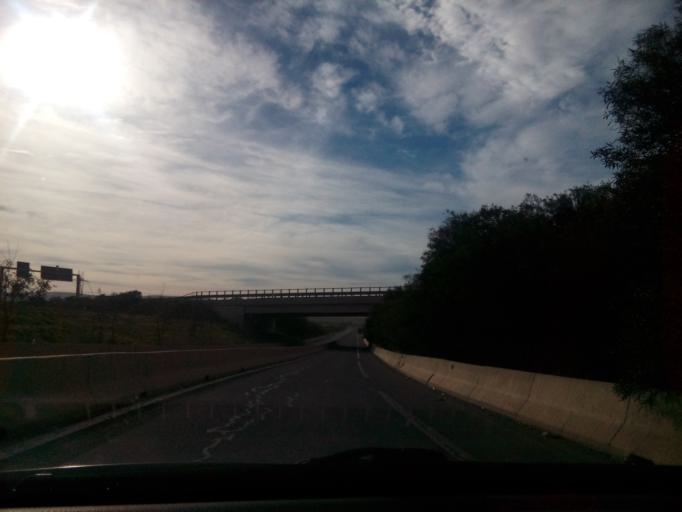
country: DZ
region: Oran
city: Sidi ech Chahmi
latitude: 35.5449
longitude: -0.3786
